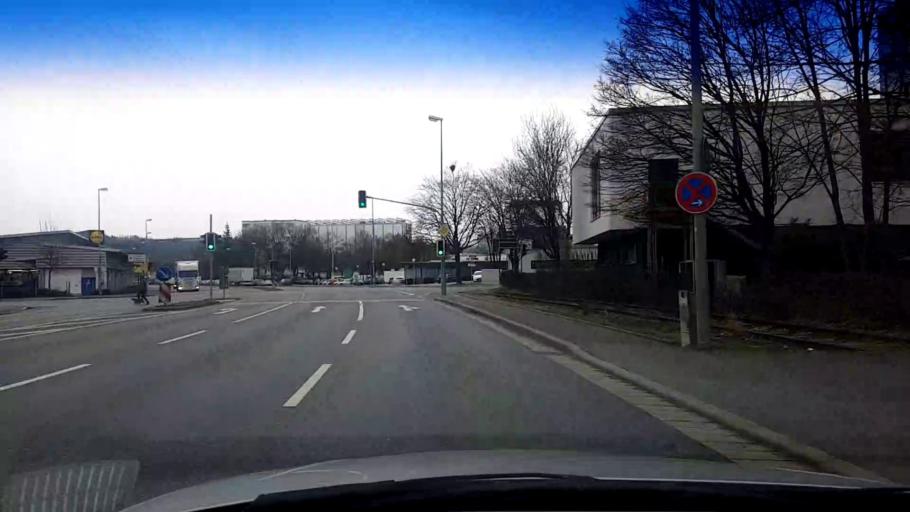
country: DE
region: Bavaria
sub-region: Upper Franconia
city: Kulmbach
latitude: 50.1022
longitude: 11.4415
